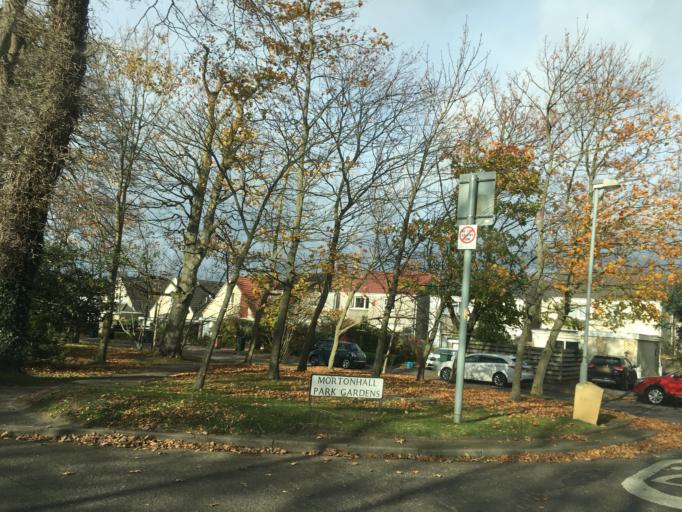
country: GB
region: Scotland
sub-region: Midlothian
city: Loanhead
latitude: 55.8995
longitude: -3.1684
